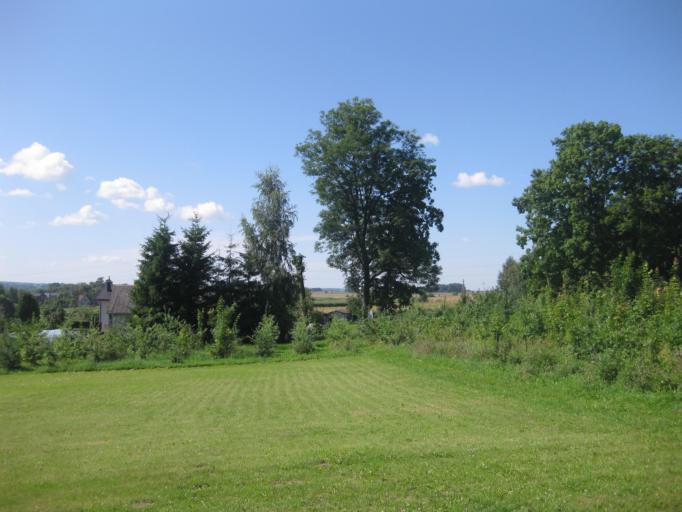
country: LT
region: Kauno apskritis
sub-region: Kauno rajonas
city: Garliava
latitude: 54.7362
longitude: 23.9241
